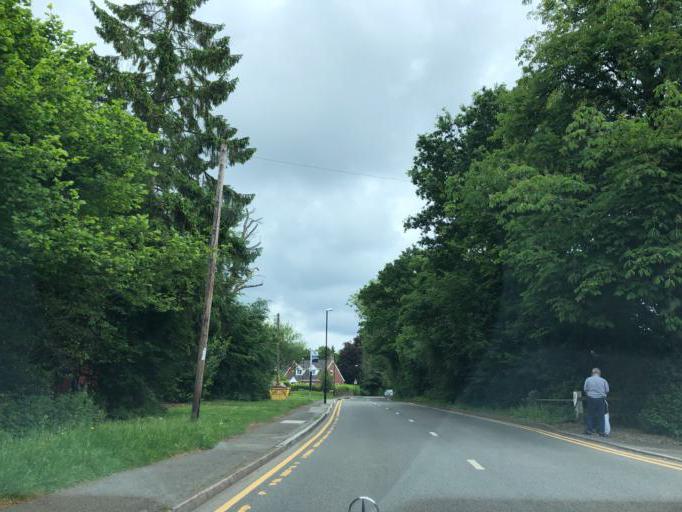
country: GB
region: England
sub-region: Solihull
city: Berkswell
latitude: 52.3963
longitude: -1.5987
